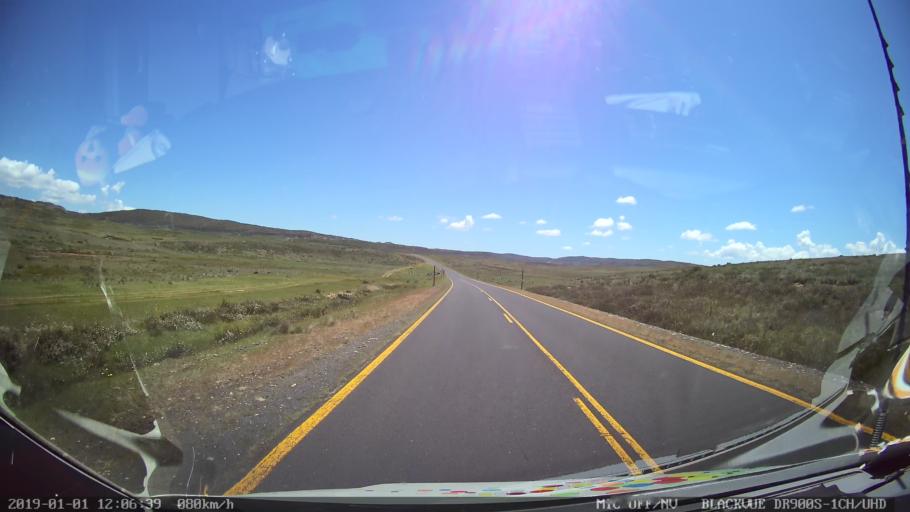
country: AU
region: New South Wales
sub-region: Snowy River
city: Jindabyne
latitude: -35.8425
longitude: 148.4914
